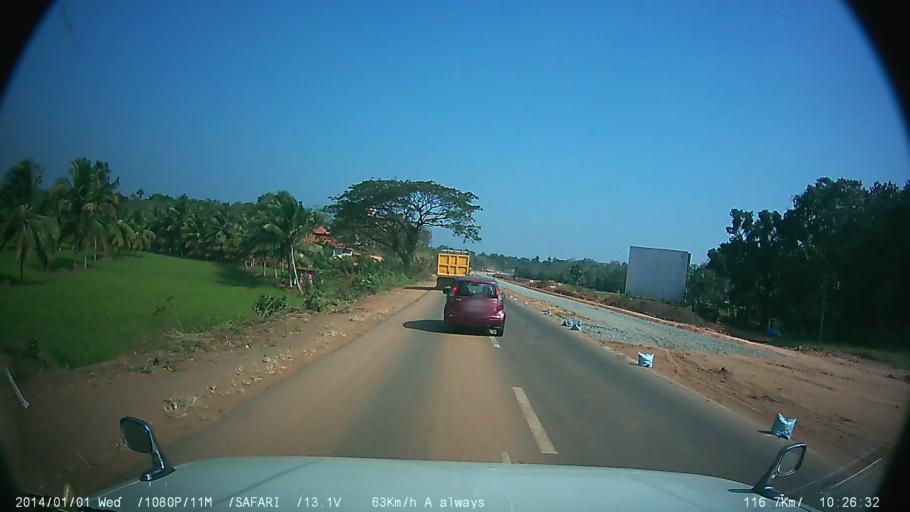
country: IN
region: Kerala
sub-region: Thrissur District
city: Chelakara
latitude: 10.6277
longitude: 76.5128
